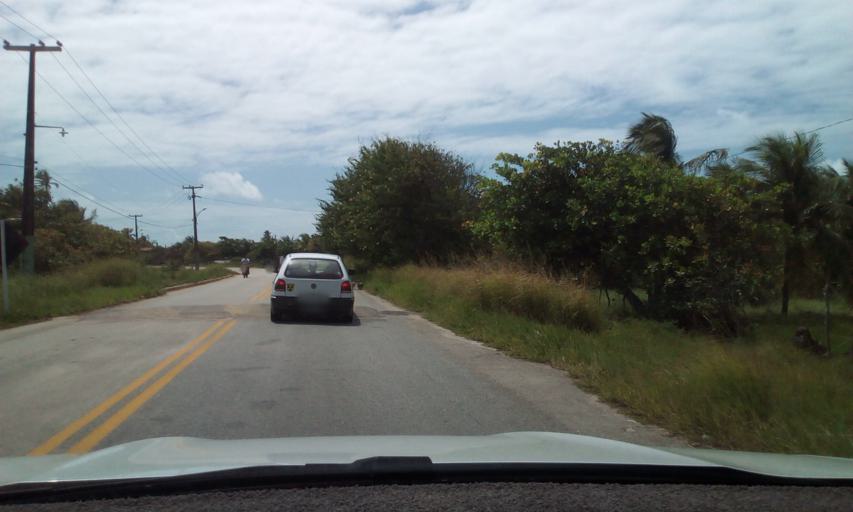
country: BR
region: Paraiba
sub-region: Rio Tinto
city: Rio Tinto
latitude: -6.7083
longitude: -34.9362
